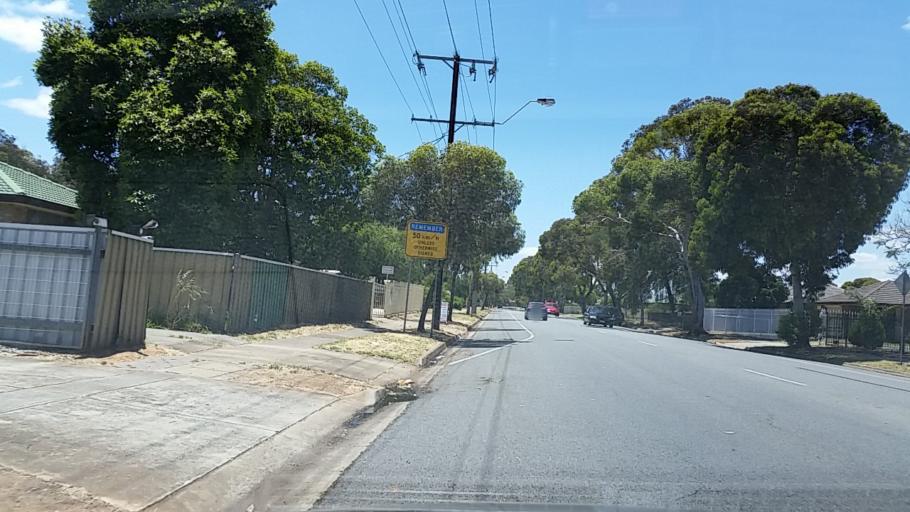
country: AU
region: South Australia
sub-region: Salisbury
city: Salisbury
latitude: -34.7657
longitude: 138.6263
